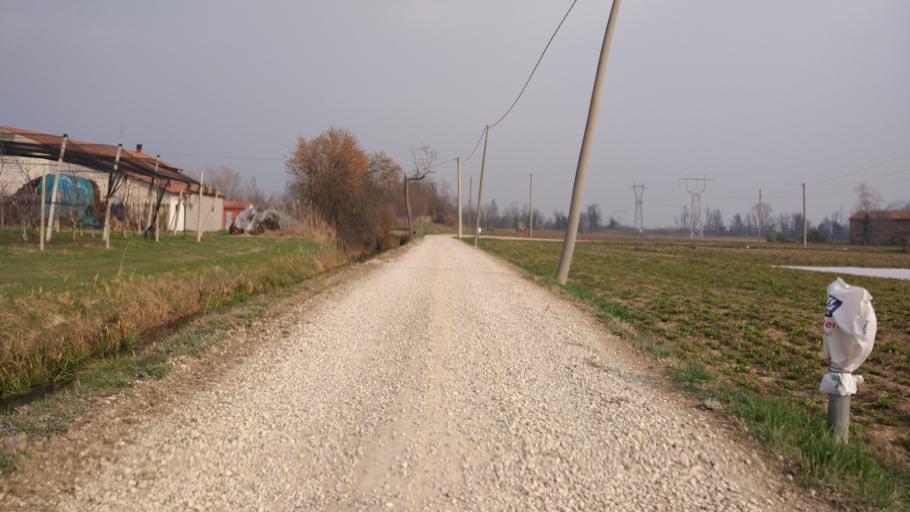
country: IT
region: Veneto
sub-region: Provincia di Verona
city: Caldierino-Rota
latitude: 45.3927
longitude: 11.1504
